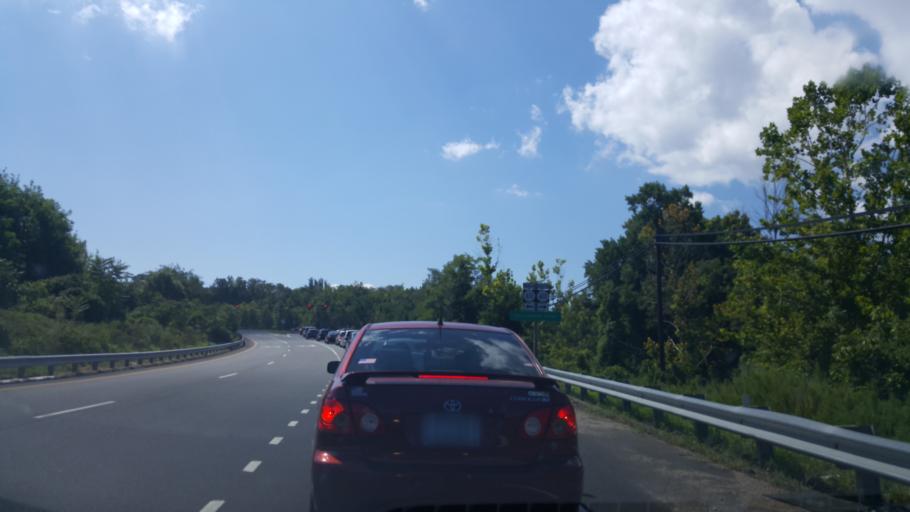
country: US
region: Virginia
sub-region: Fairfax County
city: Newington
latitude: 38.7252
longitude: -77.1850
